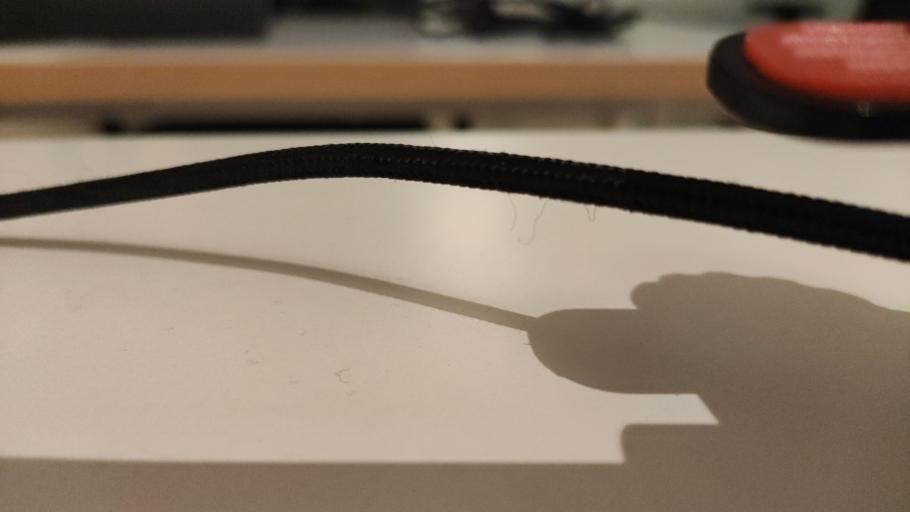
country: RU
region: Moskovskaya
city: Shaburnovo
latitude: 56.4383
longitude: 37.9124
